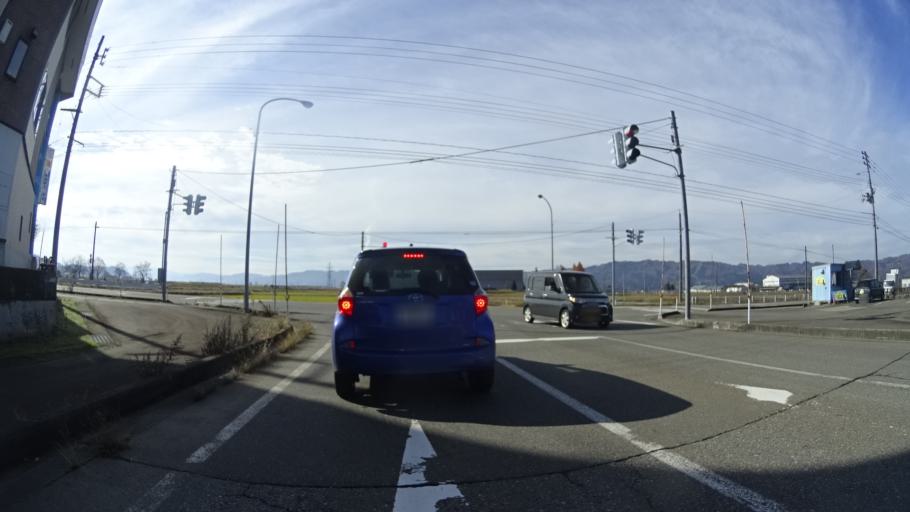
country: JP
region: Niigata
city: Muikamachi
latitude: 37.1744
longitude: 138.9677
